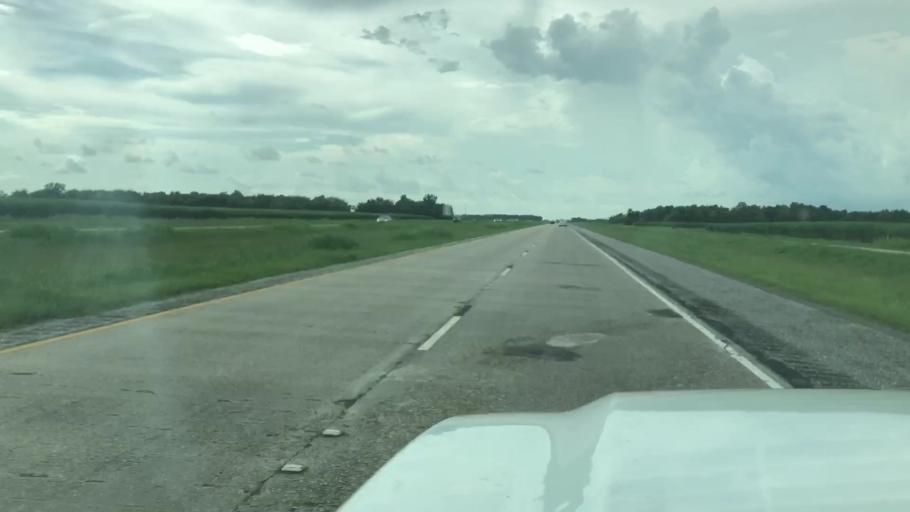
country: US
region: Louisiana
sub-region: Saint Mary Parish
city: Baldwin
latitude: 29.8448
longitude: -91.5839
